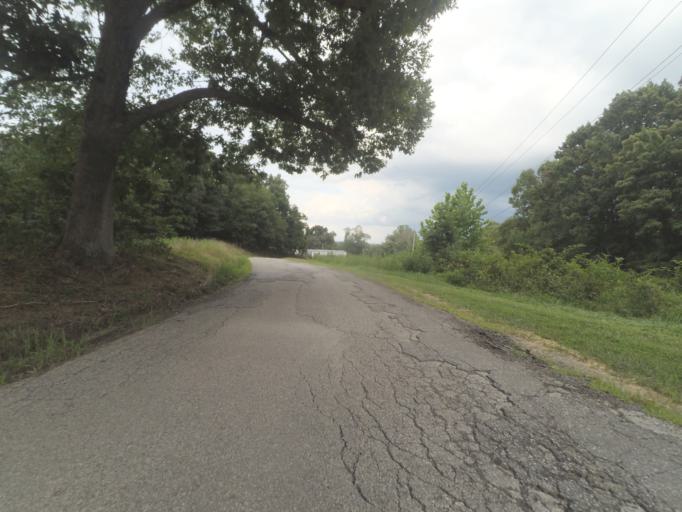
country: US
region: West Virginia
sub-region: Cabell County
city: Huntington
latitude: 38.3842
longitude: -82.4195
